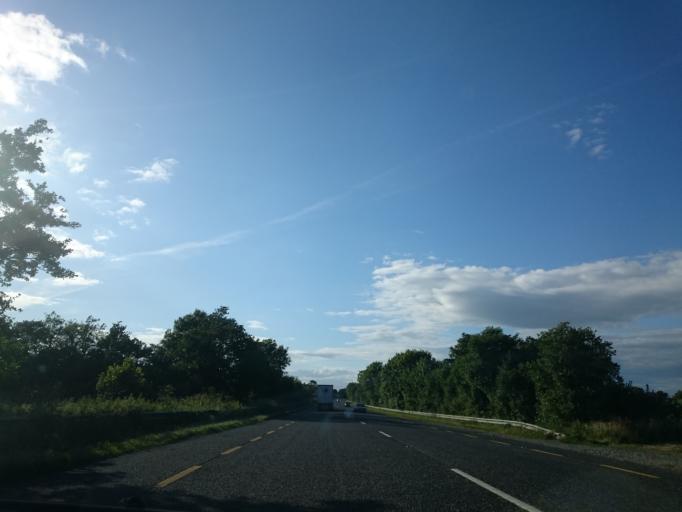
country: IE
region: Leinster
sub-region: Loch Garman
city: Loch Garman
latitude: 52.3331
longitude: -6.5113
